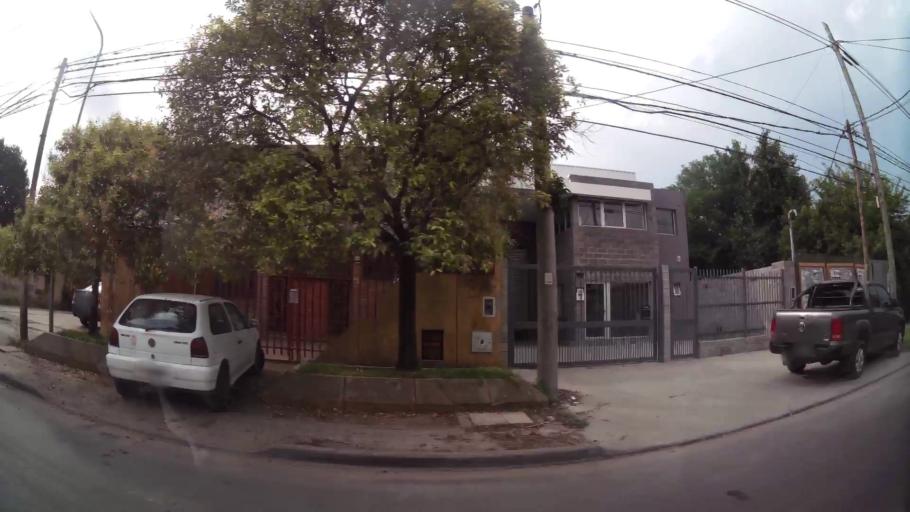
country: AR
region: Buenos Aires
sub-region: Partido de Tigre
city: Tigre
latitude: -34.4782
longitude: -58.6286
